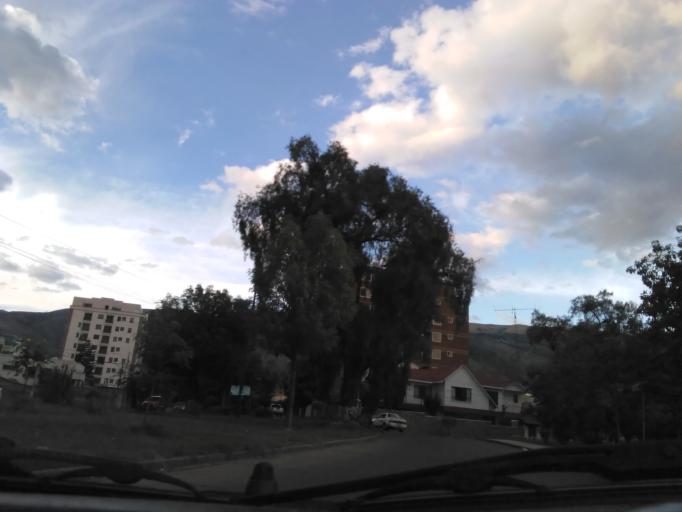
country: BO
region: Cochabamba
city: Cochabamba
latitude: -17.3701
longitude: -66.1712
